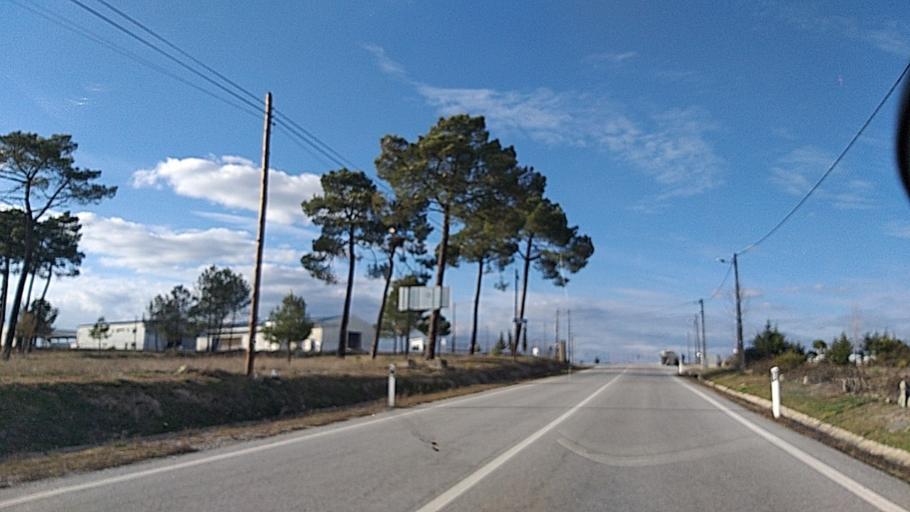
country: ES
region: Castille and Leon
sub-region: Provincia de Salamanca
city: Fuentes de Onoro
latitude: 40.6225
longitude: -6.8464
